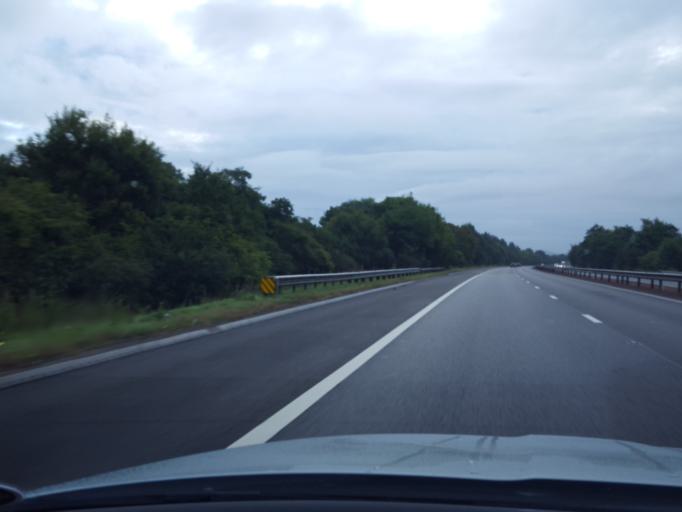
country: GB
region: Scotland
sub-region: West Lothian
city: Livingston
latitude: 55.9198
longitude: -3.5009
